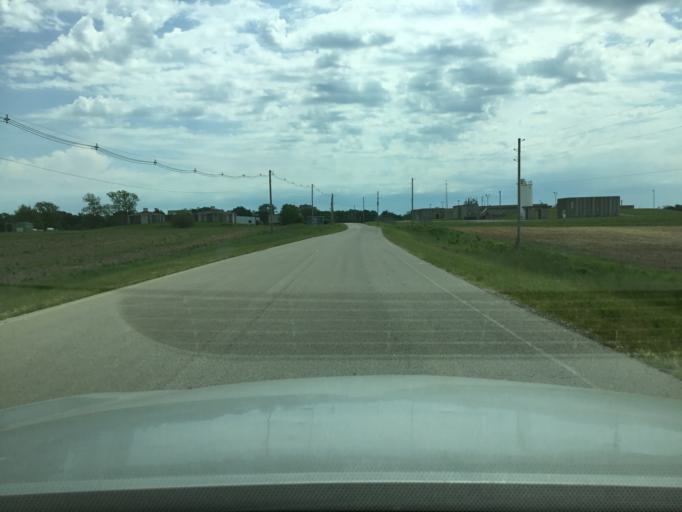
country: US
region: Kansas
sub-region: Montgomery County
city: Coffeyville
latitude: 37.0072
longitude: -95.6123
